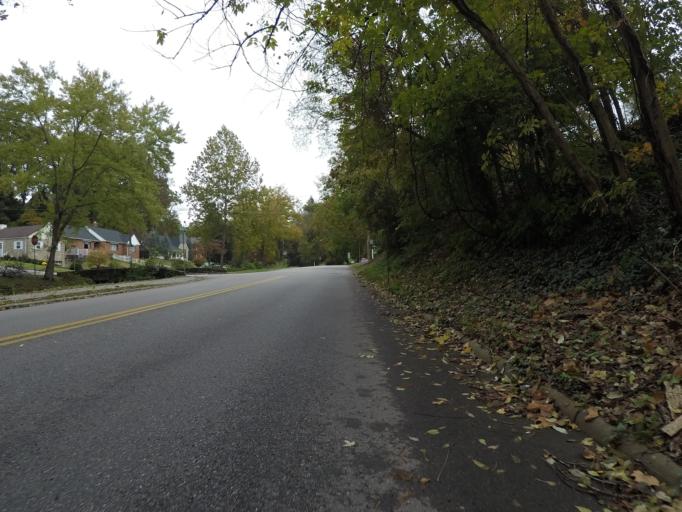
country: US
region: West Virginia
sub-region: Cabell County
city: Huntington
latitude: 38.4020
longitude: -82.4175
